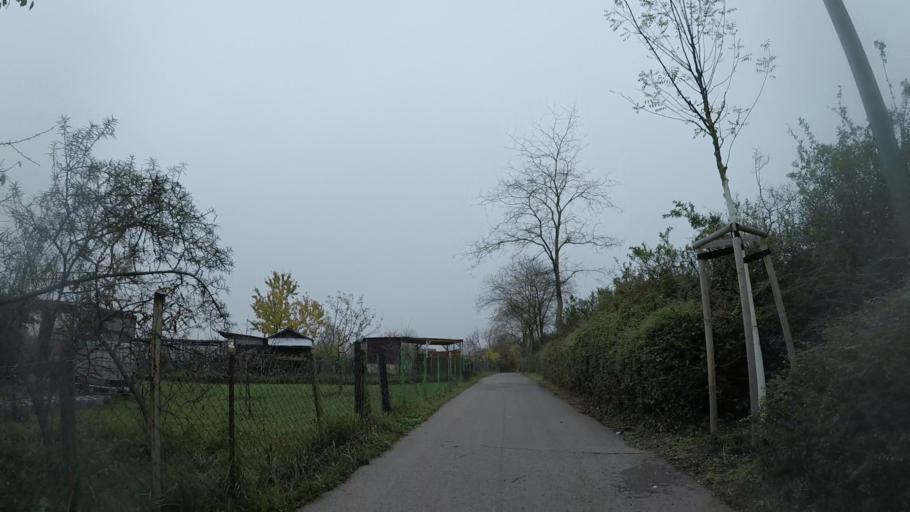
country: DE
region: Baden-Wuerttemberg
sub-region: Tuebingen Region
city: Reutlingen
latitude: 48.5176
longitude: 9.2174
